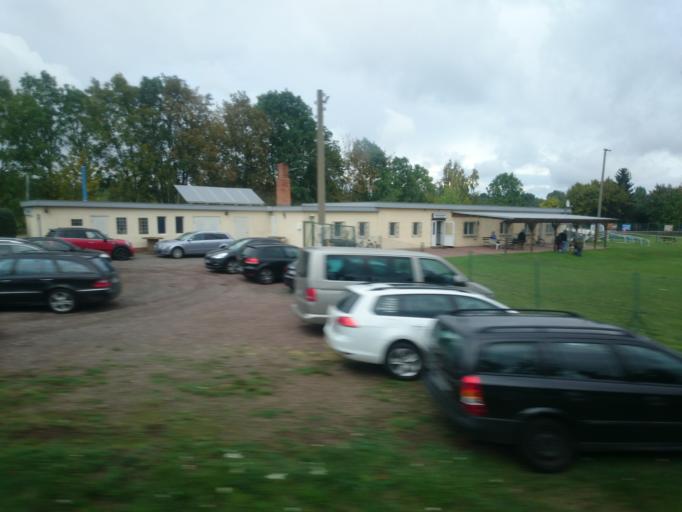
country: DE
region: Saxony-Anhalt
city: Dieskau
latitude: 51.4431
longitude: 12.0346
